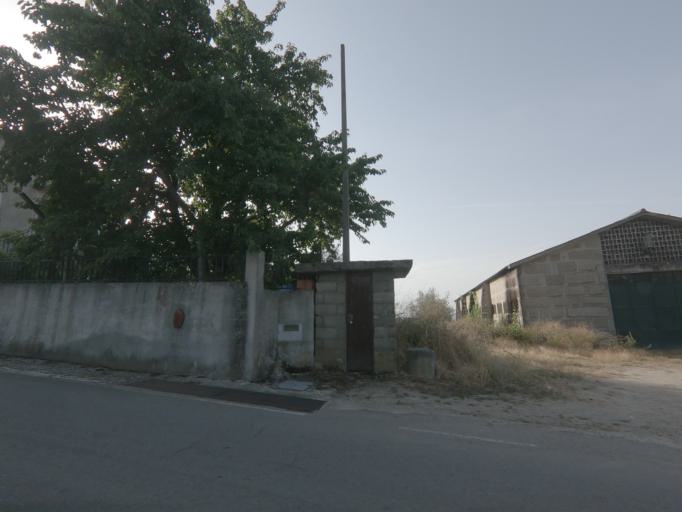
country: PT
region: Viseu
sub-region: Sao Joao da Pesqueira
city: Sao Joao da Pesqueira
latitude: 41.2304
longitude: -7.4686
